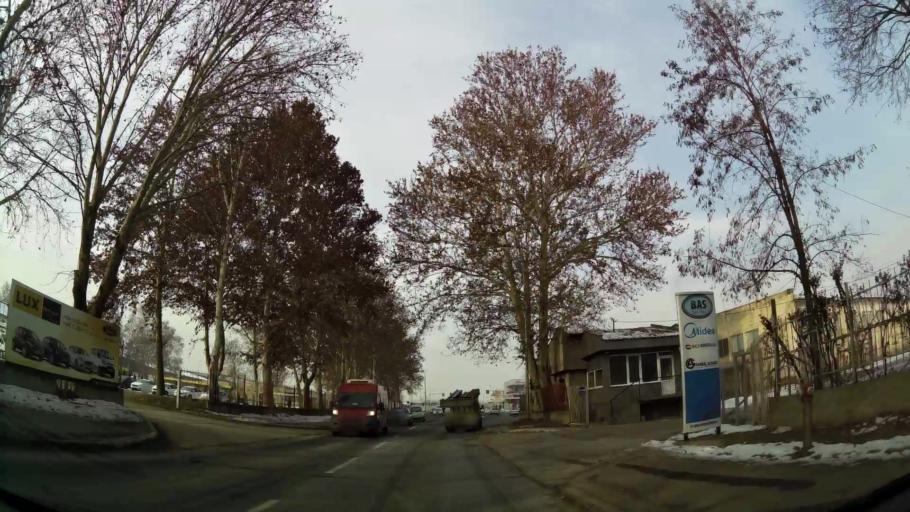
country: MK
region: Cair
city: Cair
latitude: 42.0252
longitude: 21.4315
